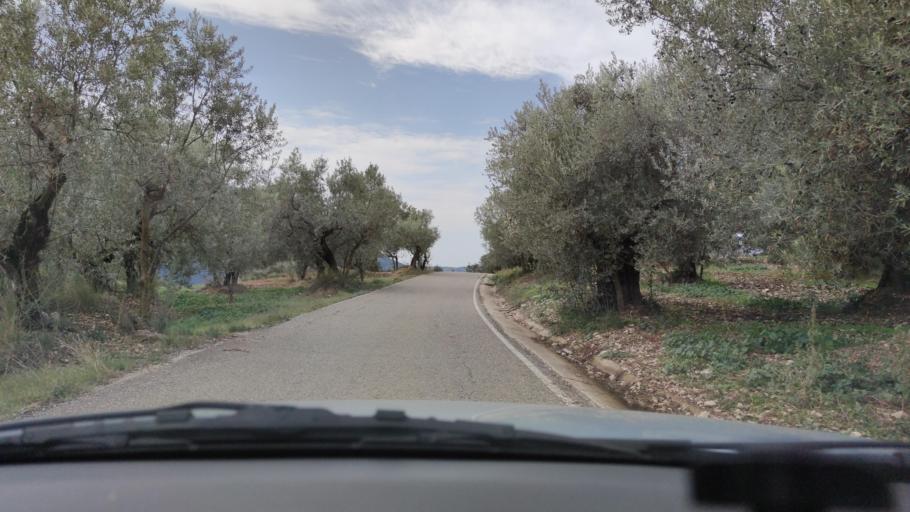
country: ES
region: Catalonia
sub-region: Provincia de Lleida
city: Llimiana
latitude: 42.0694
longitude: 0.9386
